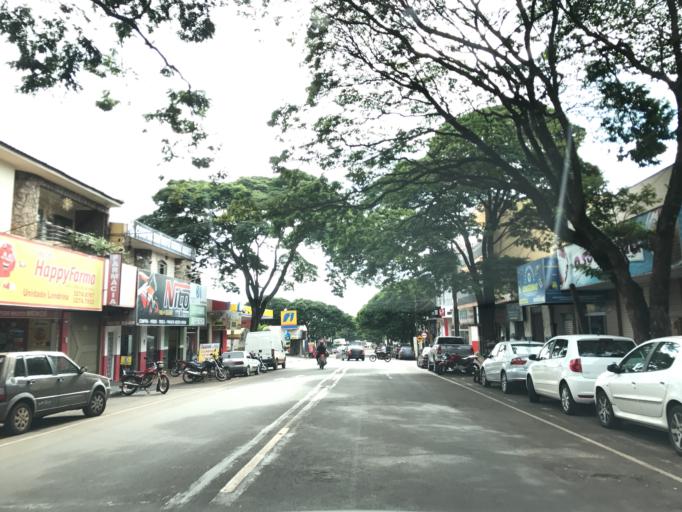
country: BR
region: Parana
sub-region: Sarandi
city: Sarandi
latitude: -23.4364
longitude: -51.8691
